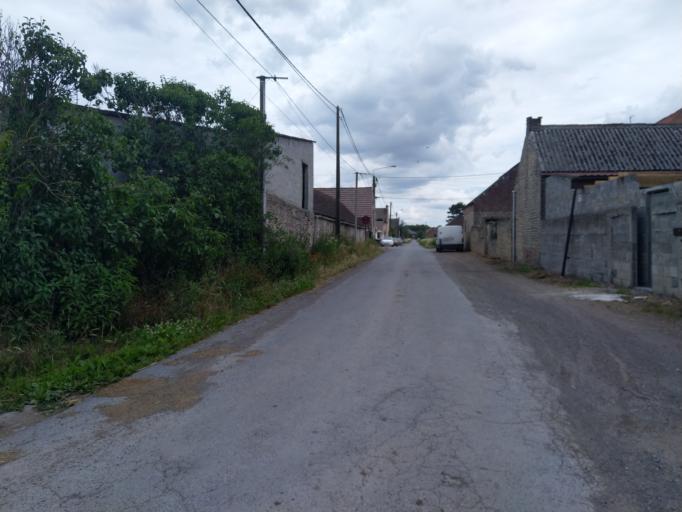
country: BE
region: Wallonia
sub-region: Province du Hainaut
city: Bernissart
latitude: 50.4719
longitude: 3.6296
